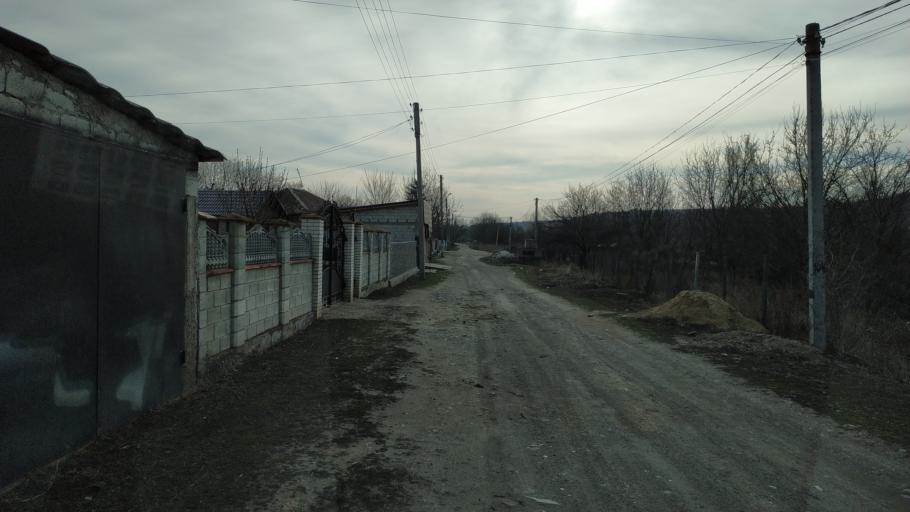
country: MD
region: Chisinau
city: Vatra
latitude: 46.9815
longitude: 28.6738
